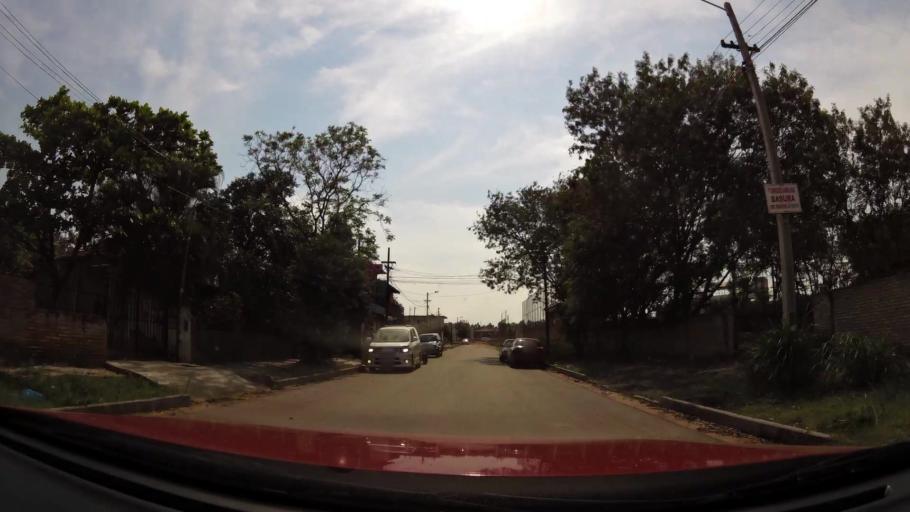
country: PY
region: Central
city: Fernando de la Mora
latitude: -25.2748
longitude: -57.5473
